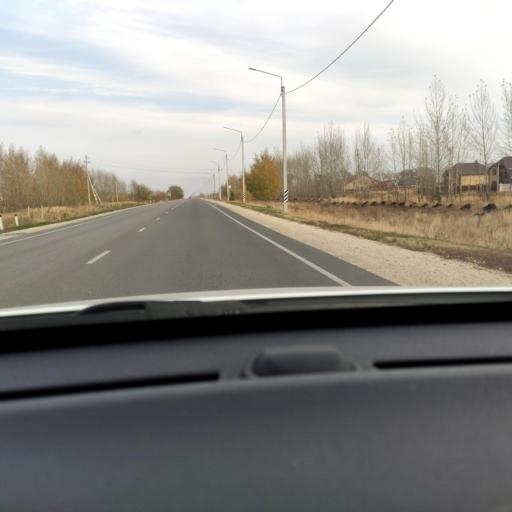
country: RU
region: Voronezj
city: Novaya Usman'
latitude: 51.6672
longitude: 39.4535
